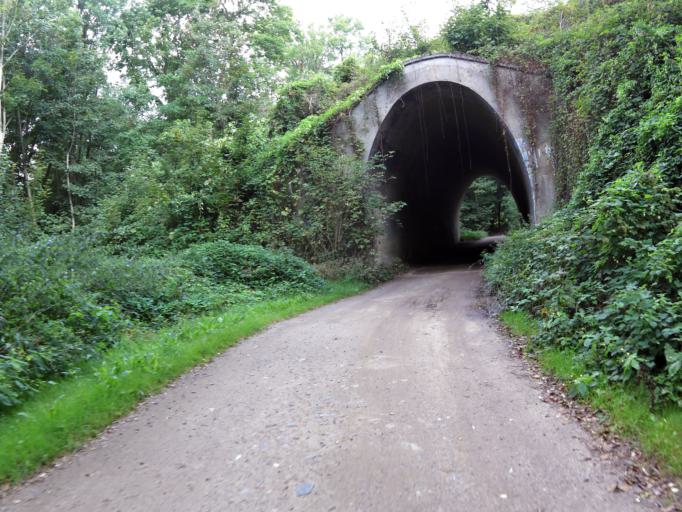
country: DE
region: Mecklenburg-Vorpommern
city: Seebad Bansin
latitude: 53.9747
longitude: 14.1065
